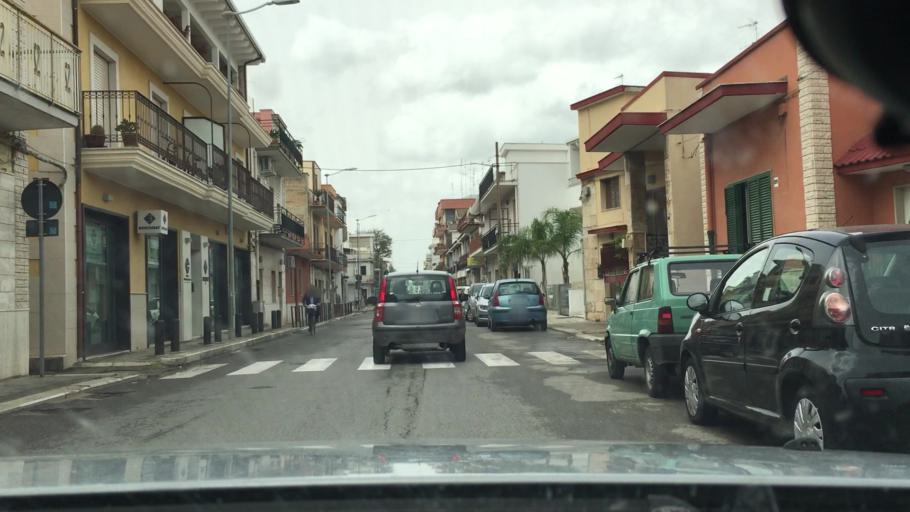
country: IT
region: Apulia
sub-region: Provincia di Bari
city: Capurso
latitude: 41.0475
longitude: 16.9267
